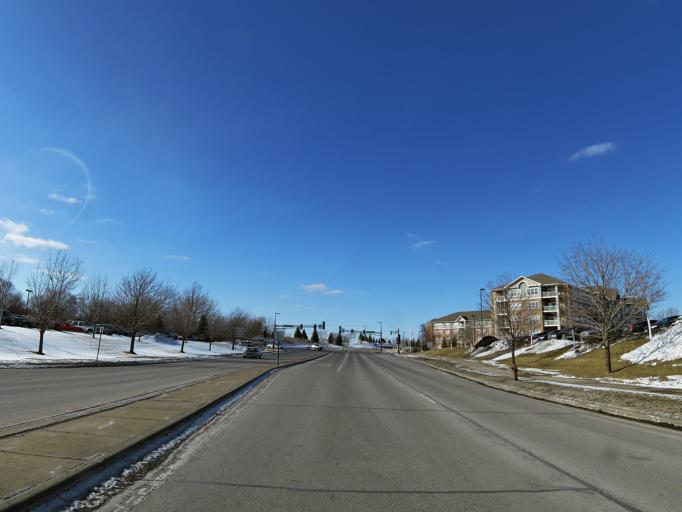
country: US
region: Minnesota
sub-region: Washington County
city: Woodbury
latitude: 44.9181
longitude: -92.9820
